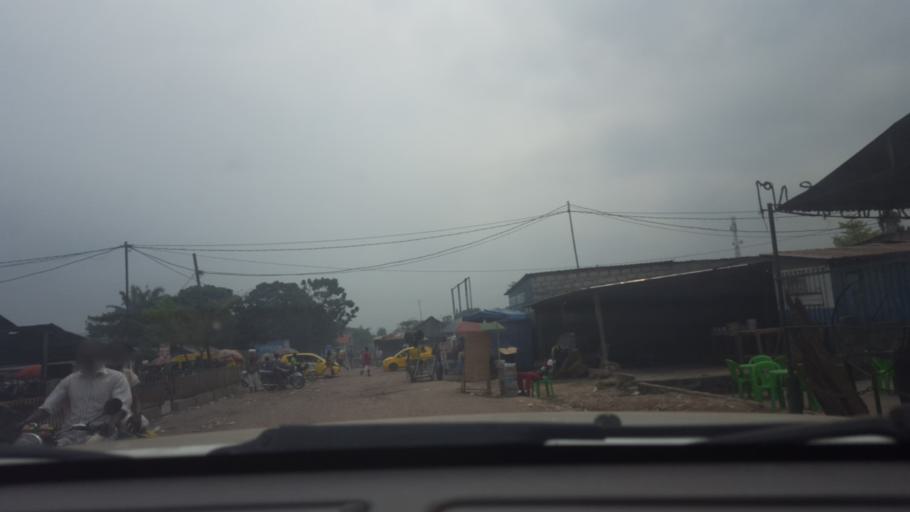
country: CD
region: Kinshasa
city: Masina
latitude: -4.3218
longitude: 15.5121
